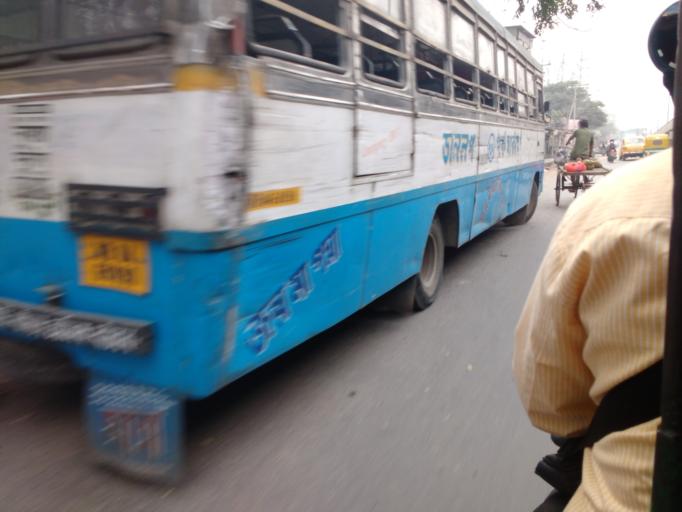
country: IN
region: West Bengal
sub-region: North 24 Parganas
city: Baranagar
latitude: 22.6523
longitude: 88.3761
